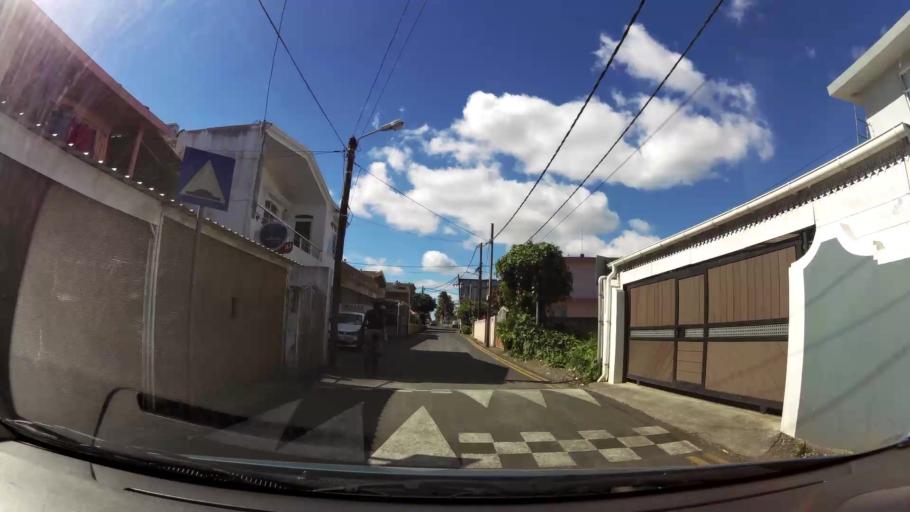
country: MU
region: Plaines Wilhems
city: Vacoas
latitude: -20.2912
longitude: 57.4813
